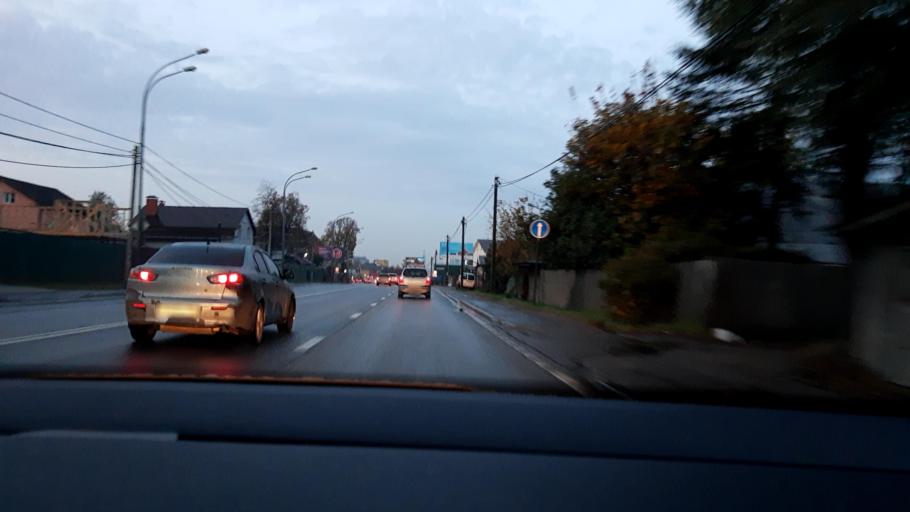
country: RU
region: Moscow
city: Vostochnyy
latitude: 55.8189
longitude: 37.8540
